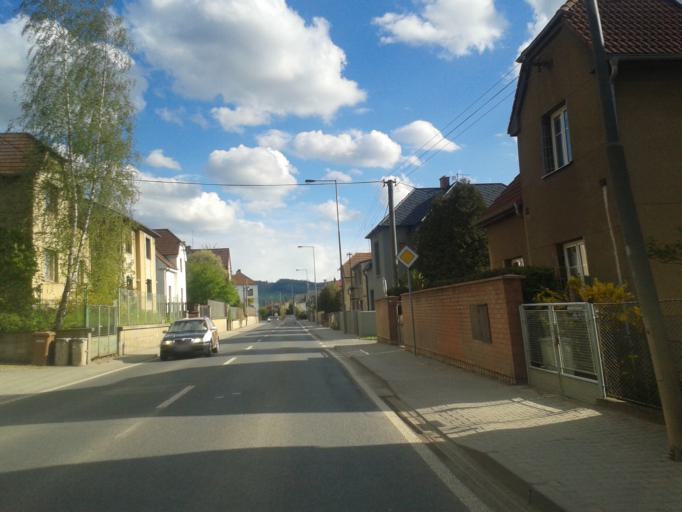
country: CZ
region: Central Bohemia
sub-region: Okres Beroun
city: Beroun
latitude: 49.9757
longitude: 14.0753
